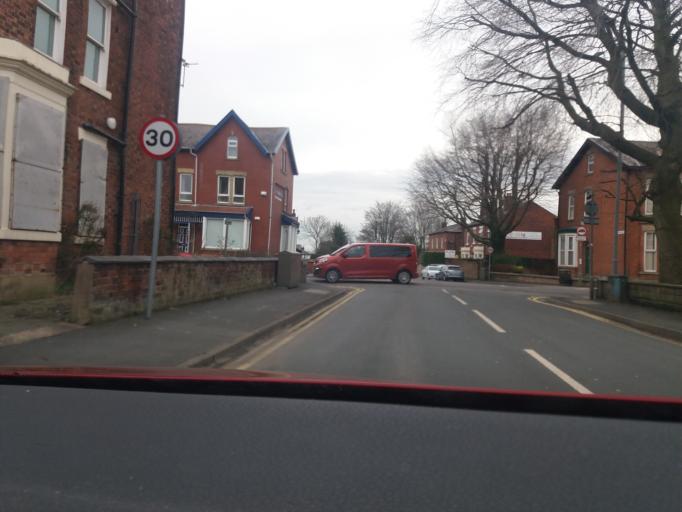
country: GB
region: England
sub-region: Lancashire
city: Chorley
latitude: 53.6532
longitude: -2.6375
